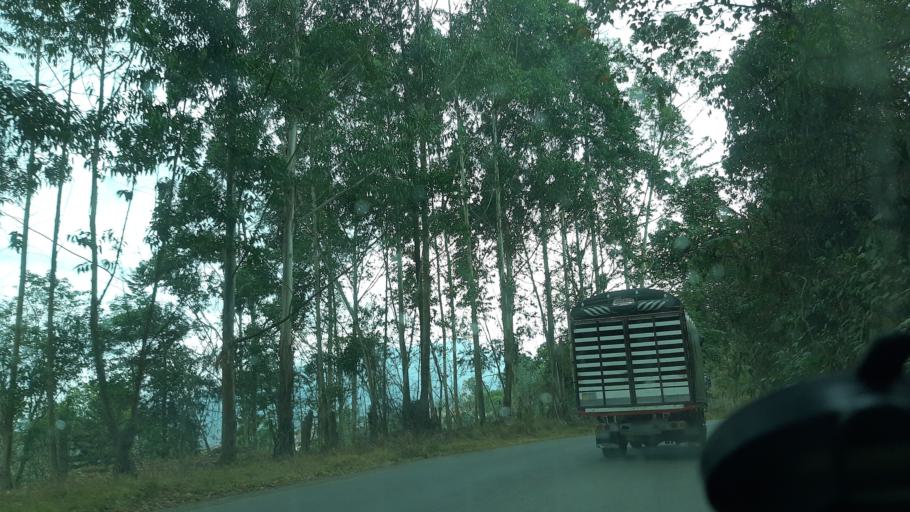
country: CO
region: Boyaca
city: Garagoa
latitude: 5.0780
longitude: -73.3719
